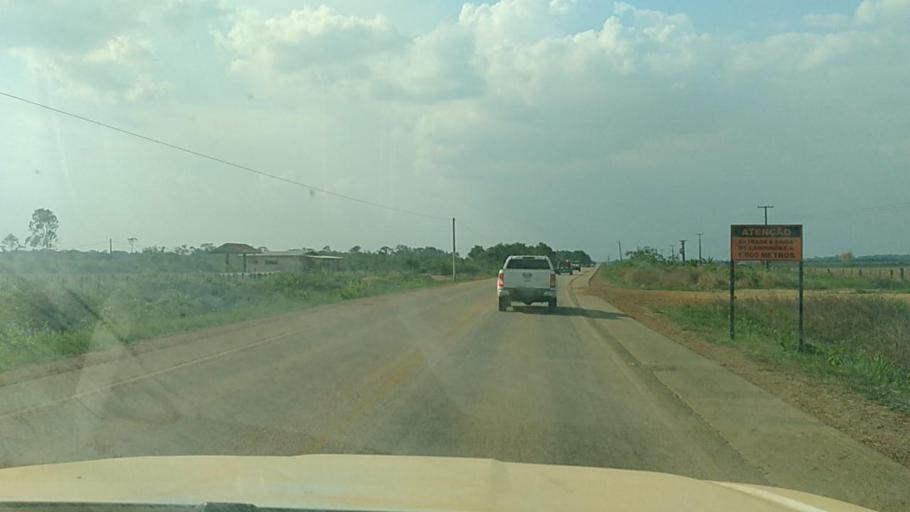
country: BR
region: Rondonia
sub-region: Porto Velho
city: Porto Velho
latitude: -8.6562
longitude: -63.9949
